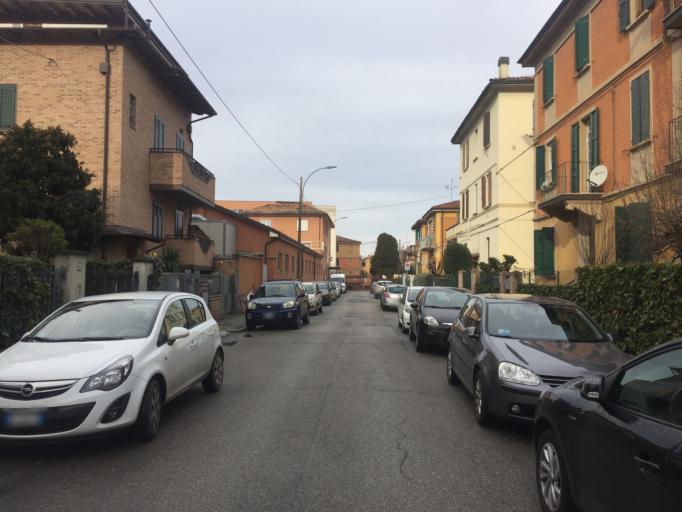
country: IT
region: Emilia-Romagna
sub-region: Provincia di Bologna
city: Casalecchio di Reno
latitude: 44.5050
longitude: 11.3004
